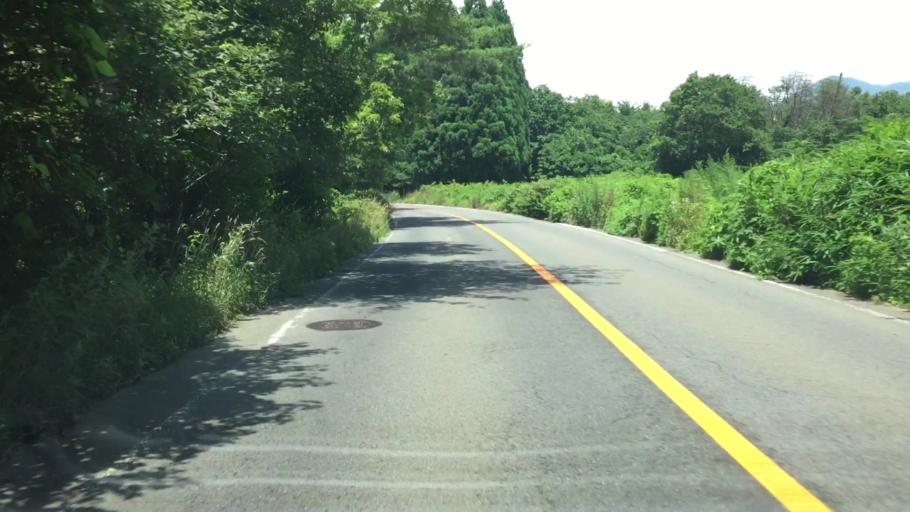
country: JP
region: Tochigi
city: Kuroiso
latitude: 37.0238
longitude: 139.9488
